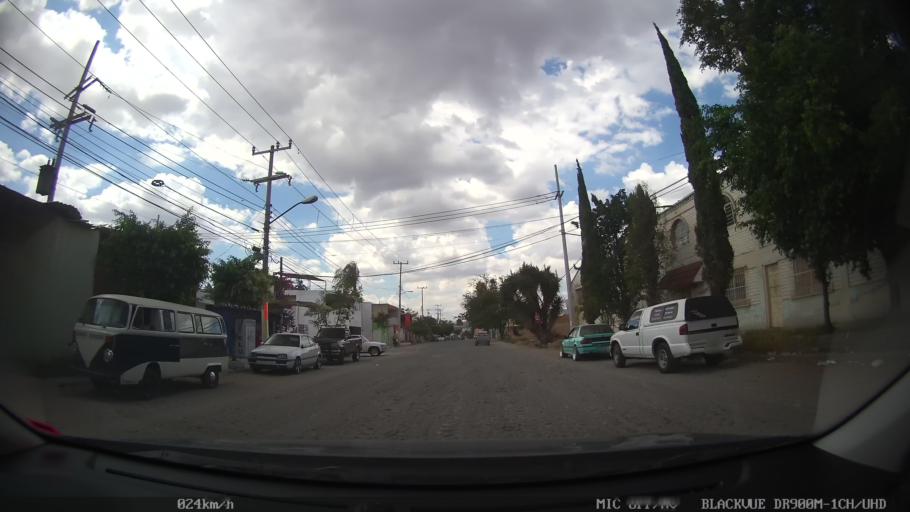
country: MX
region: Jalisco
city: Tlaquepaque
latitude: 20.6720
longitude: -103.2603
